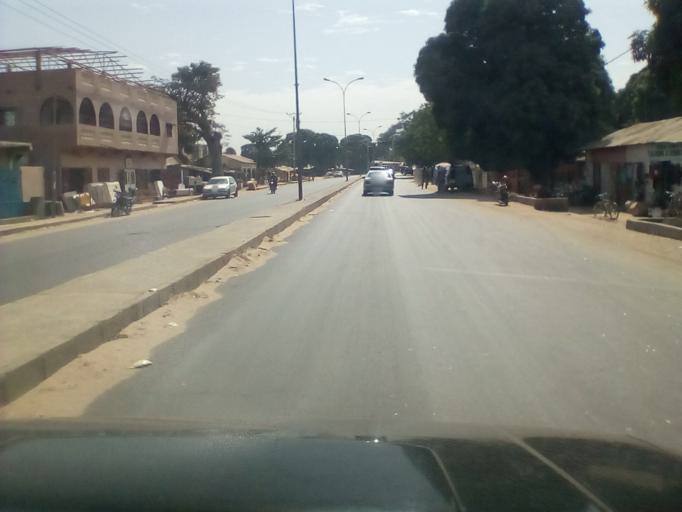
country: GM
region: Western
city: Abuko
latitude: 13.3839
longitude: -16.6437
